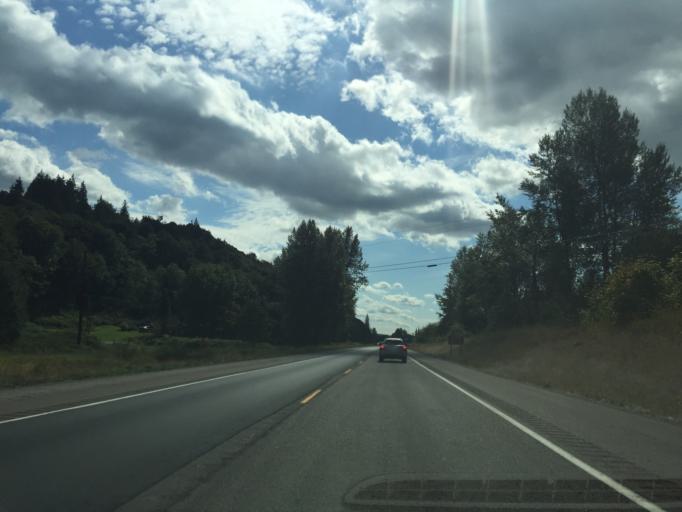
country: US
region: Washington
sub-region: Snohomish County
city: Snohomish
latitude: 47.9294
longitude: -122.0725
